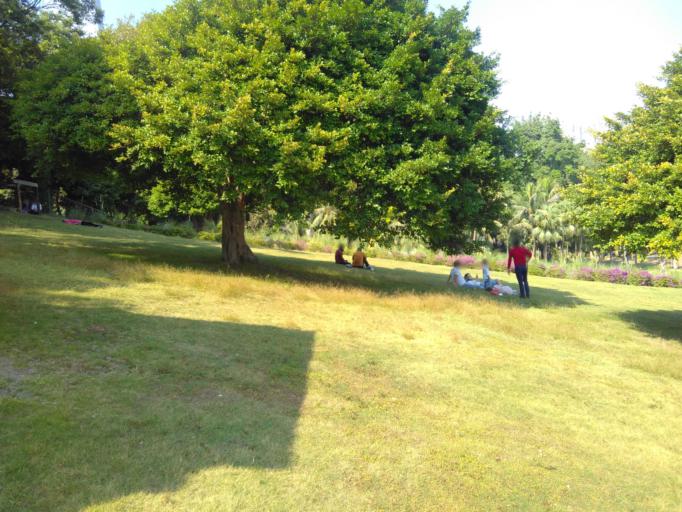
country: CN
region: Guangdong
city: Shahe
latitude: 22.5317
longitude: 113.9807
